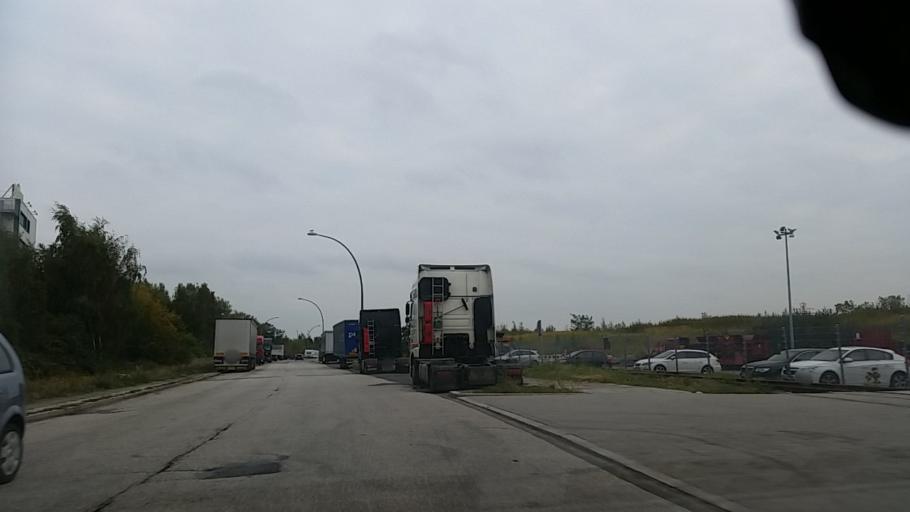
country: DE
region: Hamburg
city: Marienthal
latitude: 53.5173
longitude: 10.0889
